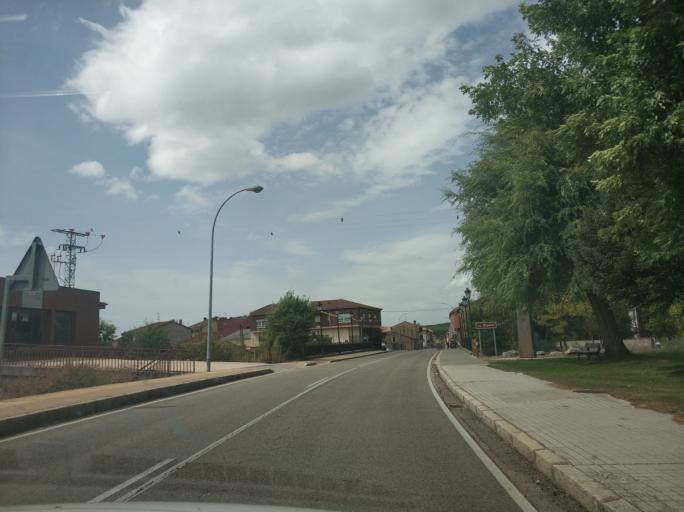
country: ES
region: Castille and Leon
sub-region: Provincia de Soria
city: Duruelo de la Sierra
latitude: 41.9526
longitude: -2.9285
